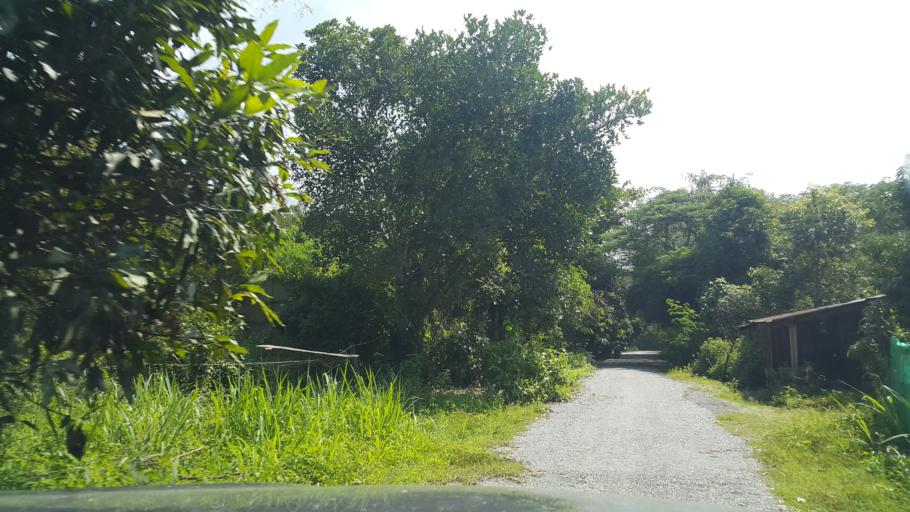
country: TH
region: Chiang Mai
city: San Sai
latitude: 18.9230
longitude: 99.1329
